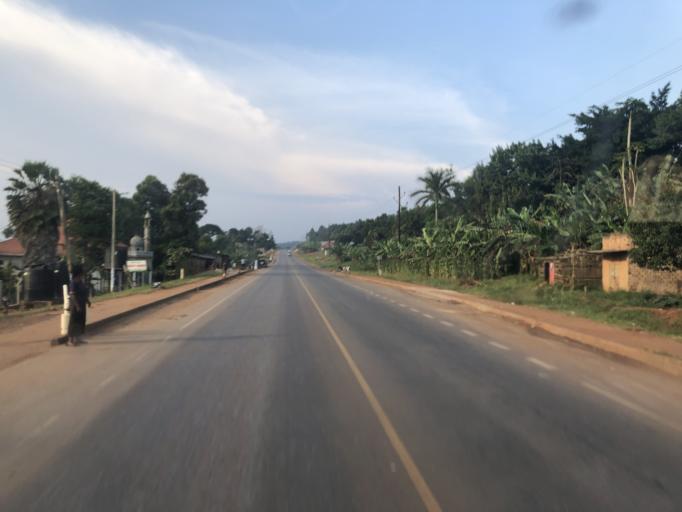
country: UG
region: Central Region
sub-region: Mpigi District
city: Mpigi
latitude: 0.1928
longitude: 32.2955
